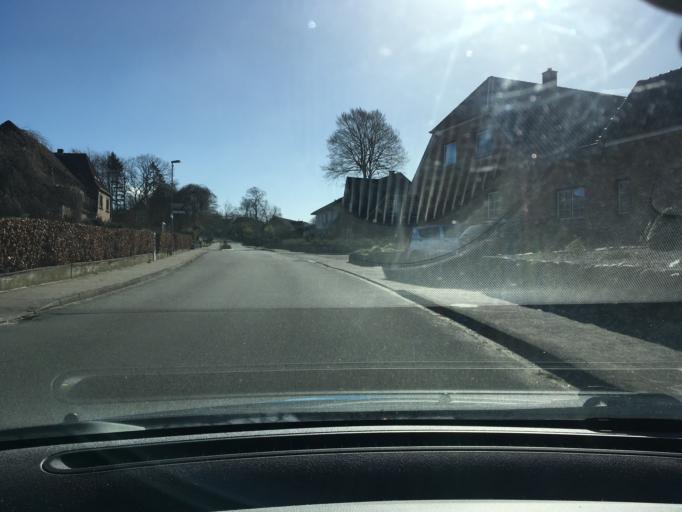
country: DE
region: Schleswig-Holstein
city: Fahrdorf
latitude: 54.5049
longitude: 9.6040
